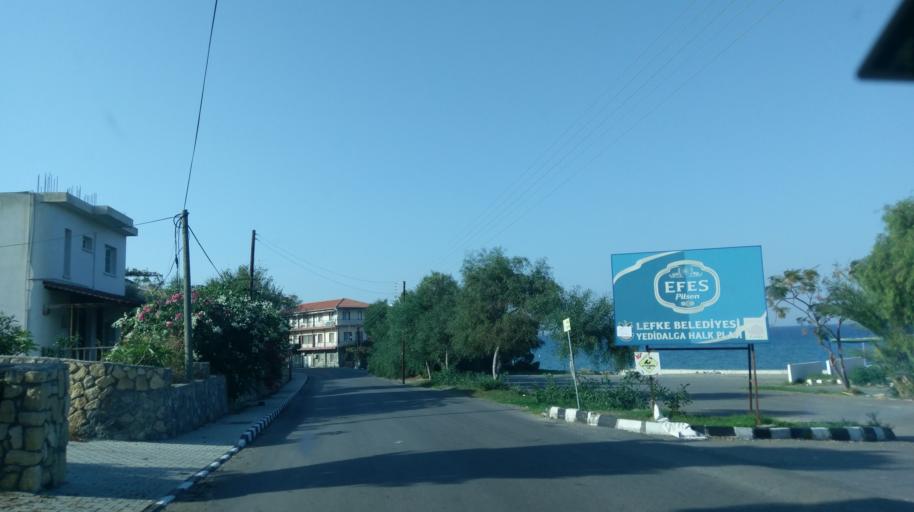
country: CY
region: Lefkosia
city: Lefka
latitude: 35.1480
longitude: 32.8031
